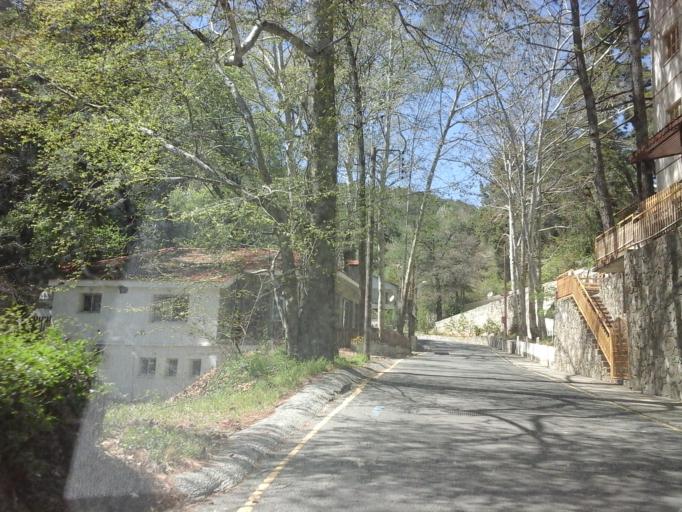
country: CY
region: Limassol
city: Pelendri
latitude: 34.8920
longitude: 32.8666
